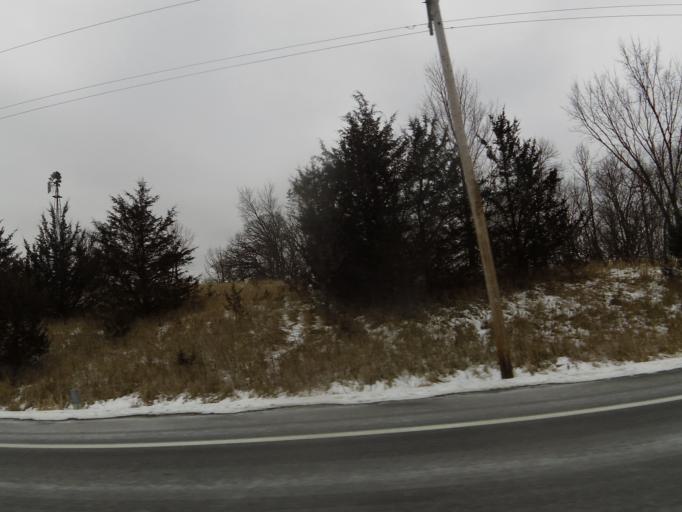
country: US
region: Minnesota
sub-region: Hennepin County
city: Medina
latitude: 45.0223
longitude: -93.6105
